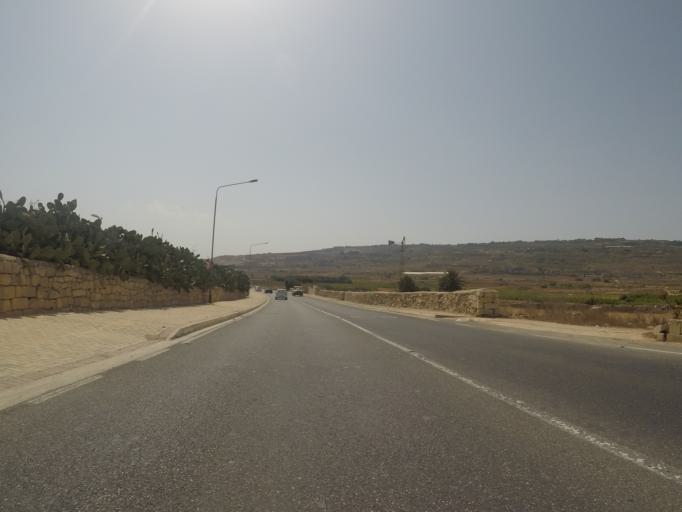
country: MT
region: L-Imgarr
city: Imgarr
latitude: 35.9180
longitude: 14.3824
